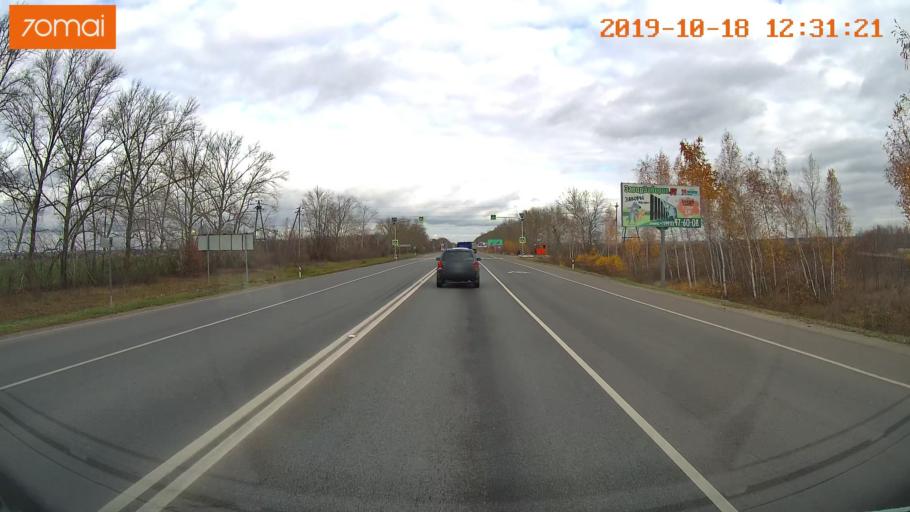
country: RU
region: Rjazan
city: Ryazan'
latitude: 54.5927
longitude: 39.6113
